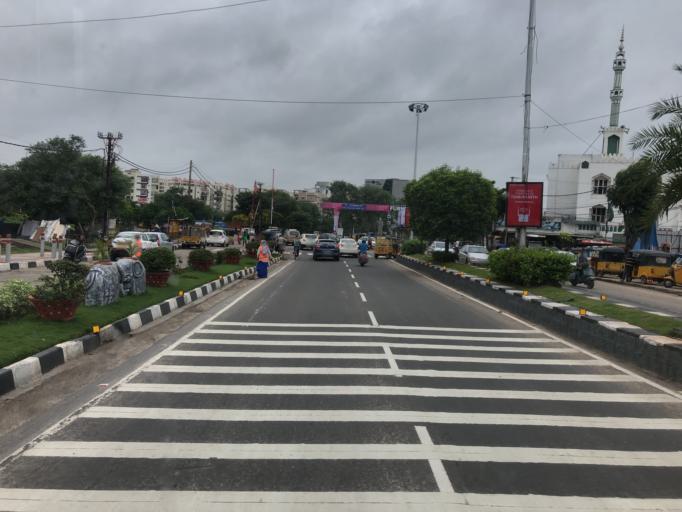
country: IN
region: Telangana
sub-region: Rangareddi
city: Kukatpalli
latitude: 17.4635
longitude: 78.3761
